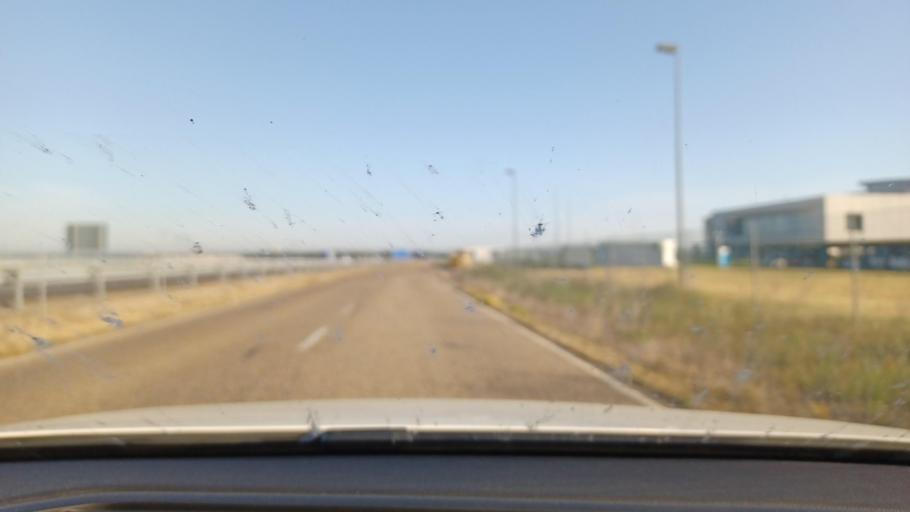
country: ES
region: Castille and Leon
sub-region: Provincia de Valladolid
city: Aldeamayor de San Martin
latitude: 41.5000
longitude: -4.6223
